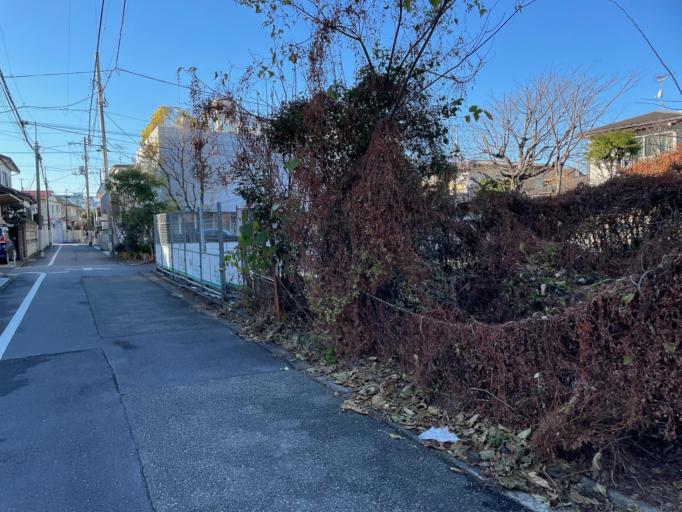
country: JP
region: Tokyo
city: Musashino
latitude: 35.7057
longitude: 139.6043
